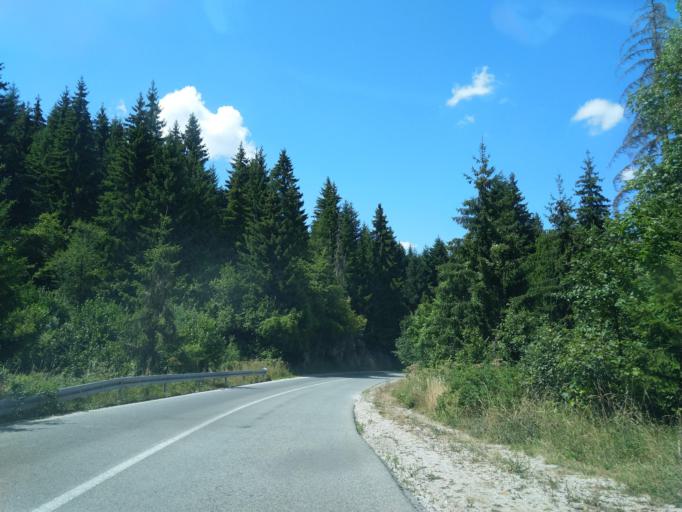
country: RS
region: Central Serbia
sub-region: Zlatiborski Okrug
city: Nova Varos
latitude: 43.4087
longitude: 19.8386
